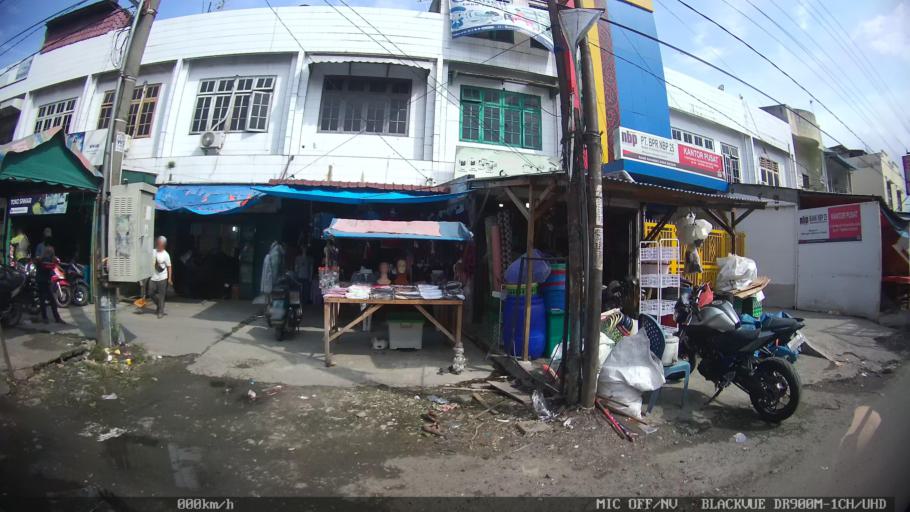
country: ID
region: North Sumatra
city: Medan
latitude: 3.5972
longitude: 98.7545
